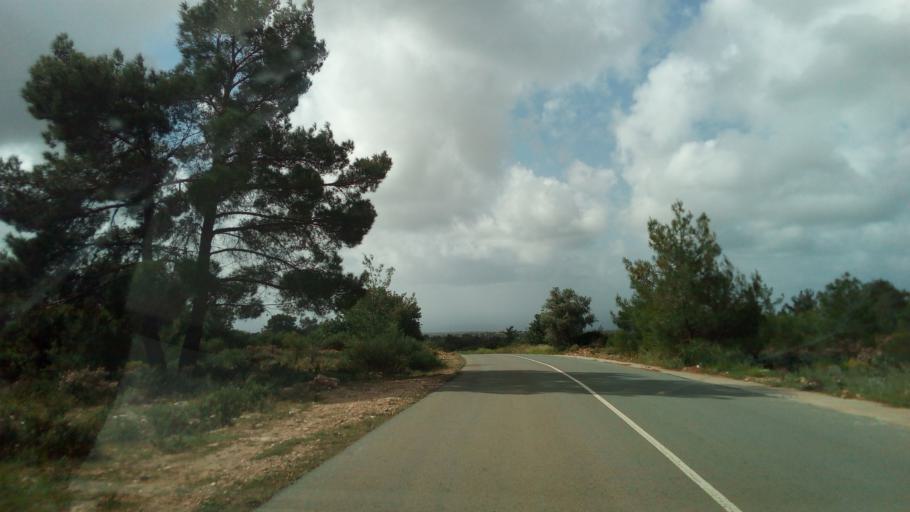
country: CY
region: Limassol
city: Sotira
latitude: 34.7276
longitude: 32.8658
